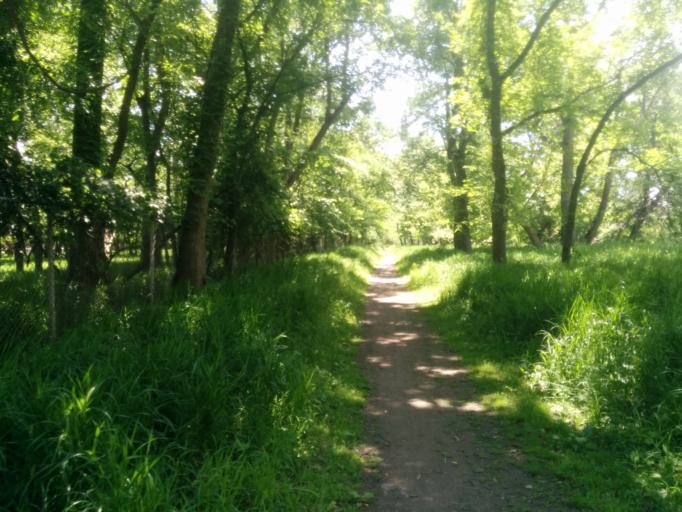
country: US
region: Illinois
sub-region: Cook County
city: Franklin Park
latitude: 41.9415
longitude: -87.8519
